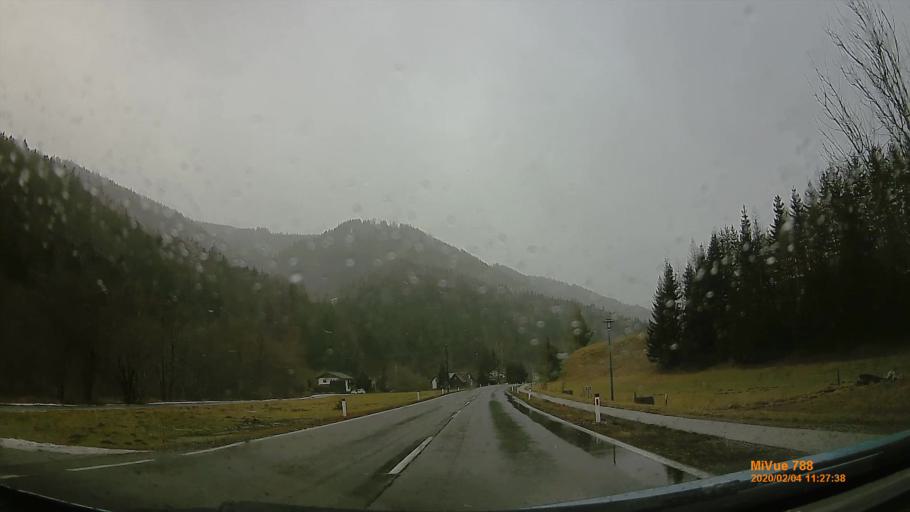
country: AT
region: Styria
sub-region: Politischer Bezirk Bruck-Muerzzuschlag
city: Kapellen
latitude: 47.6467
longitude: 15.6358
